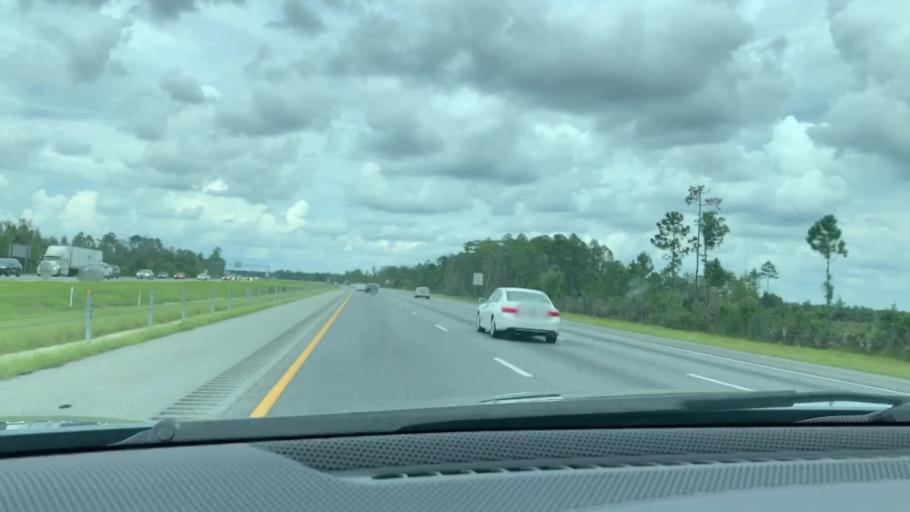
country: US
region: Georgia
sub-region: McIntosh County
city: Darien
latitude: 31.4098
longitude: -81.4449
